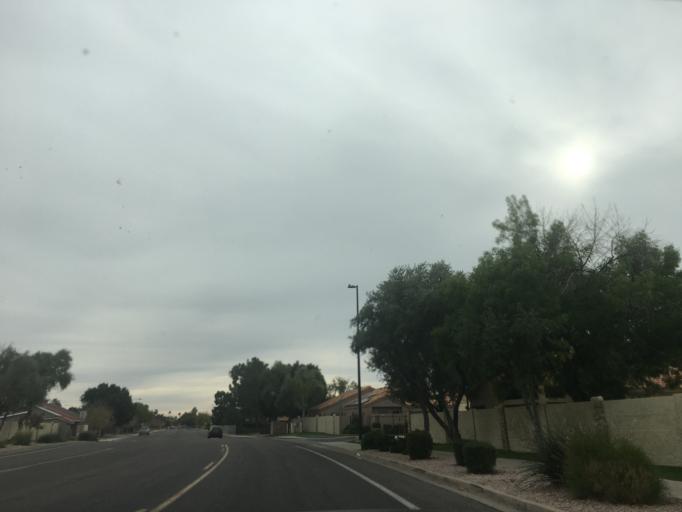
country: US
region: Arizona
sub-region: Maricopa County
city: Gilbert
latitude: 33.3545
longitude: -111.7818
